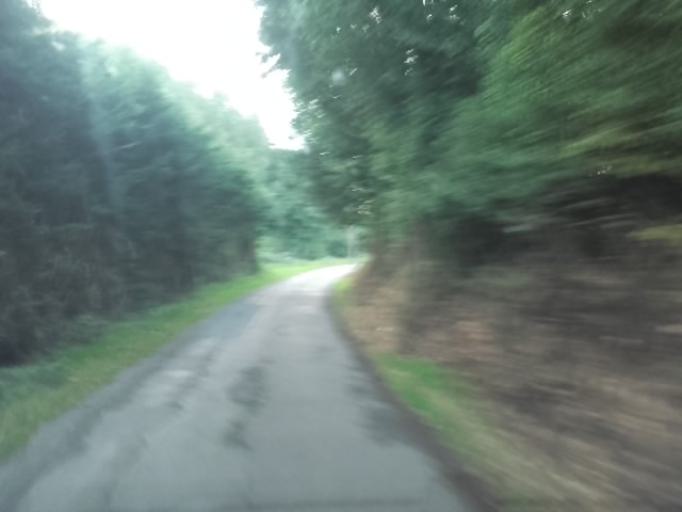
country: FR
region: Brittany
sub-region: Departement des Cotes-d'Armor
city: Pleguien
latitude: 48.6357
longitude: -2.9431
